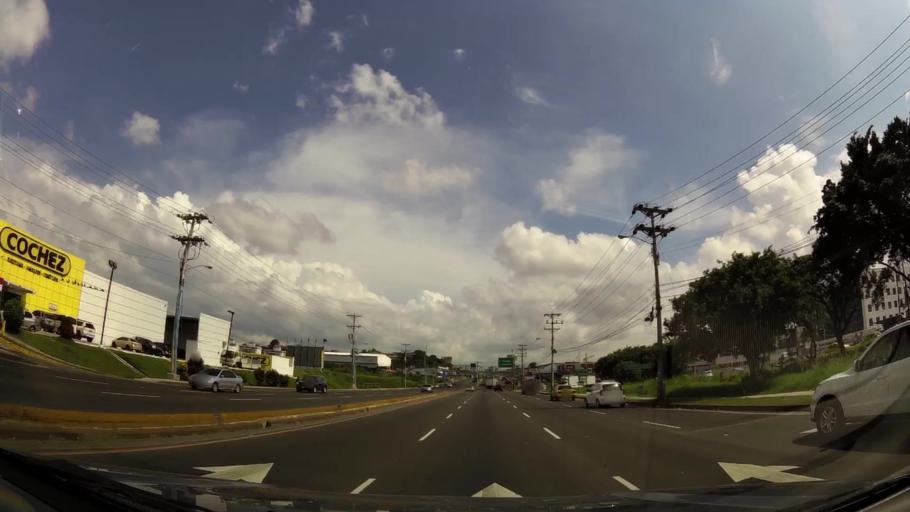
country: PA
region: Panama
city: San Miguelito
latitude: 9.0395
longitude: -79.4778
